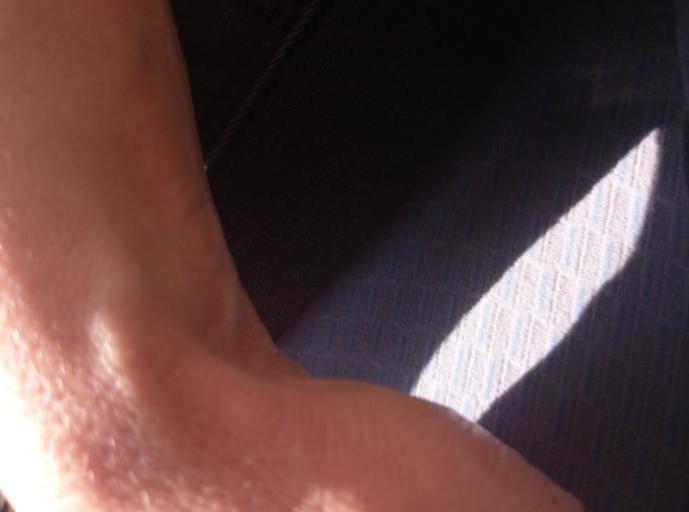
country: CD
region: Nord Kivu
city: Goma
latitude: -1.6428
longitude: 29.1685
